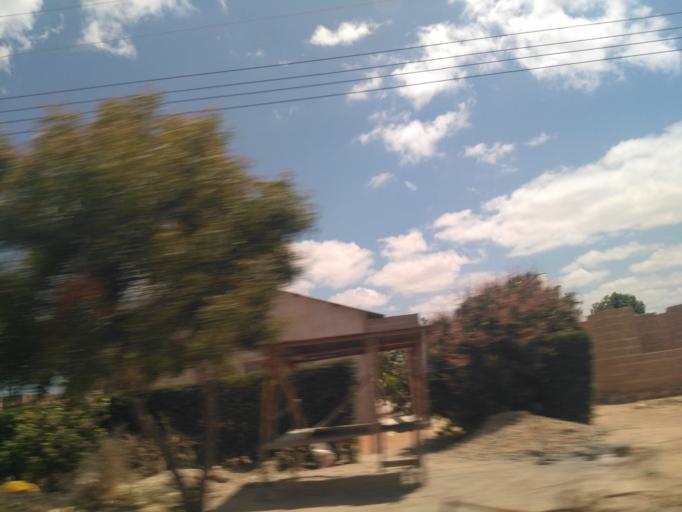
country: TZ
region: Dodoma
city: Kisasa
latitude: -6.1652
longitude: 35.7941
